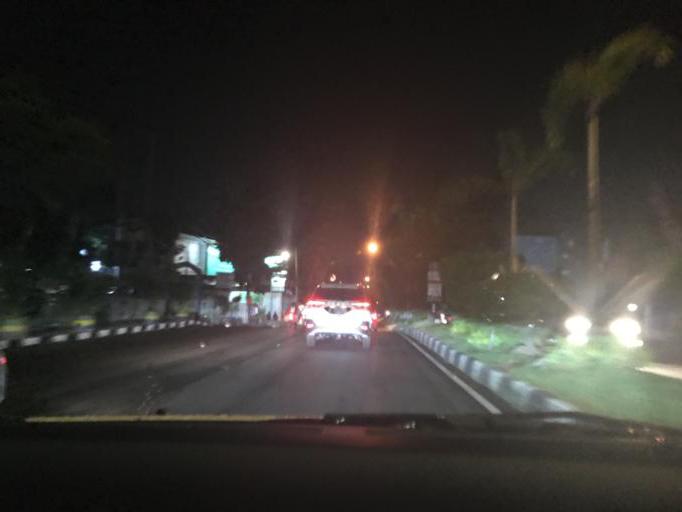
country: ID
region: West Java
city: Bandung
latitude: -6.9132
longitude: 107.6474
